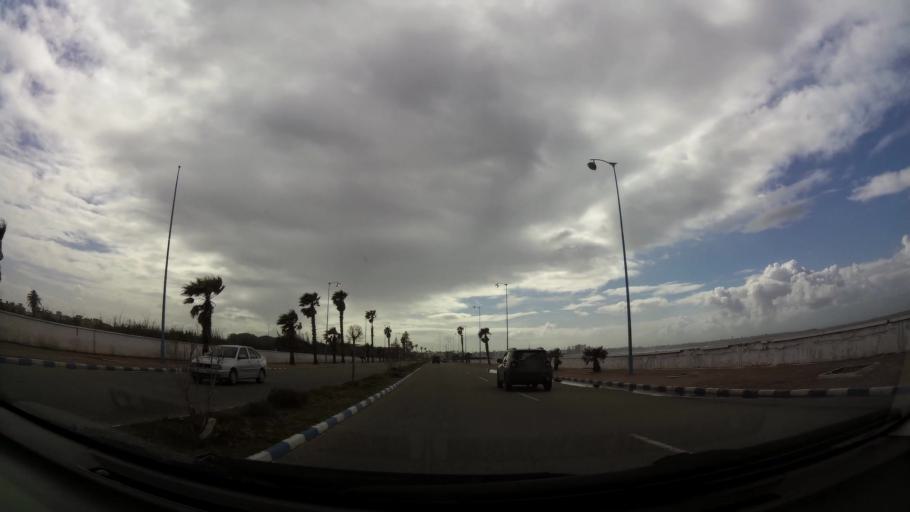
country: MA
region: Doukkala-Abda
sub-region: El-Jadida
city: El Jadida
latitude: 33.2447
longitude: -8.4801
